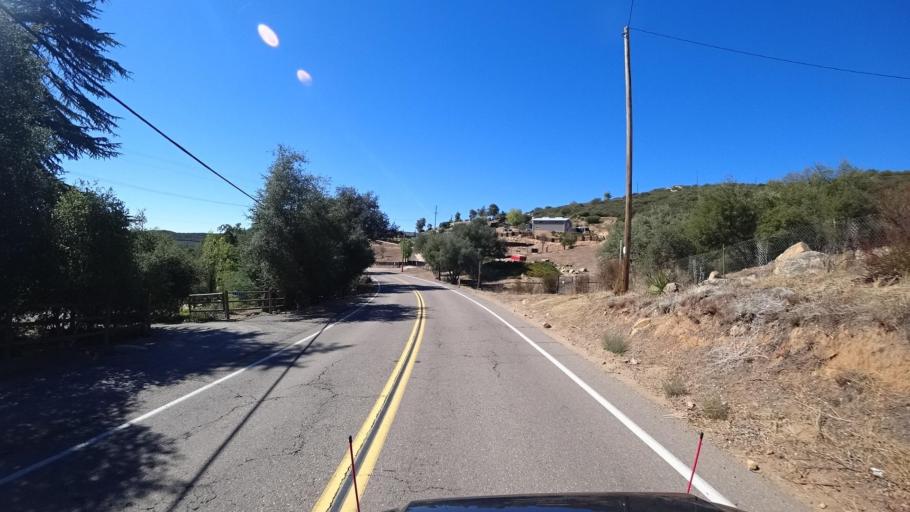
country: US
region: California
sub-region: San Diego County
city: Descanso
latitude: 32.8116
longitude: -116.6349
